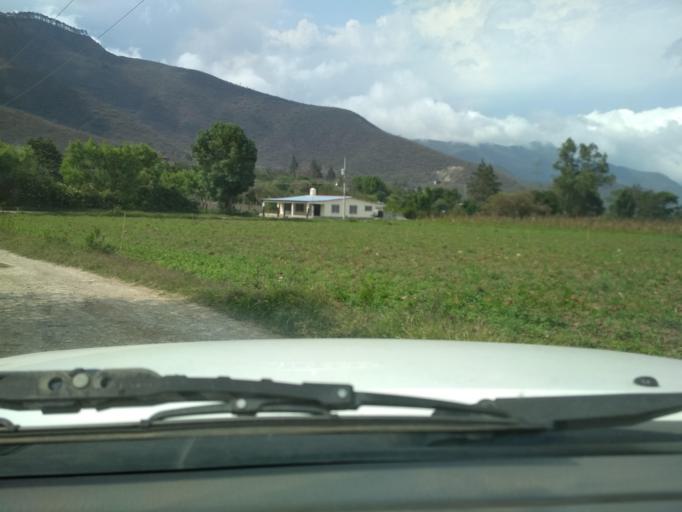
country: MX
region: Veracruz
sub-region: Acultzingo
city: Sierra de Agua
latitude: 18.7634
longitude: -97.2307
